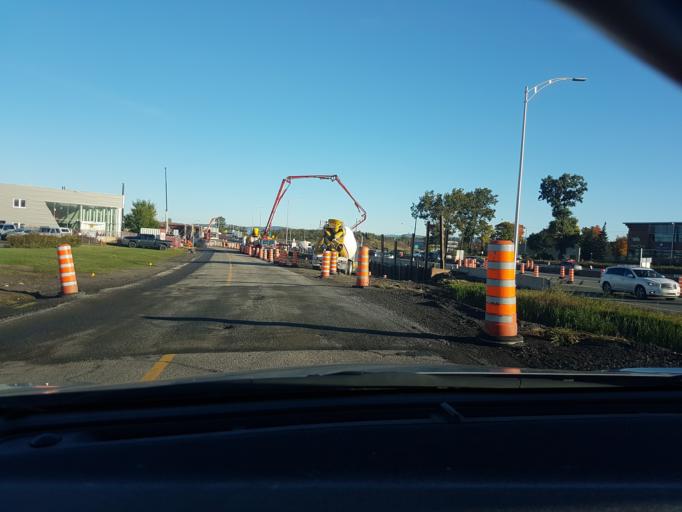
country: CA
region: Quebec
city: L'Ancienne-Lorette
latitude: 46.7918
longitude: -71.3157
